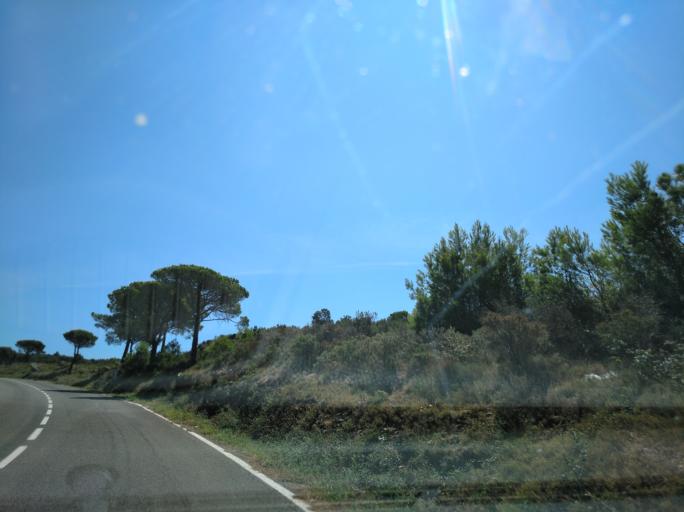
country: ES
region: Catalonia
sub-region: Provincia de Girona
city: Pau
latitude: 42.3305
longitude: 3.1319
